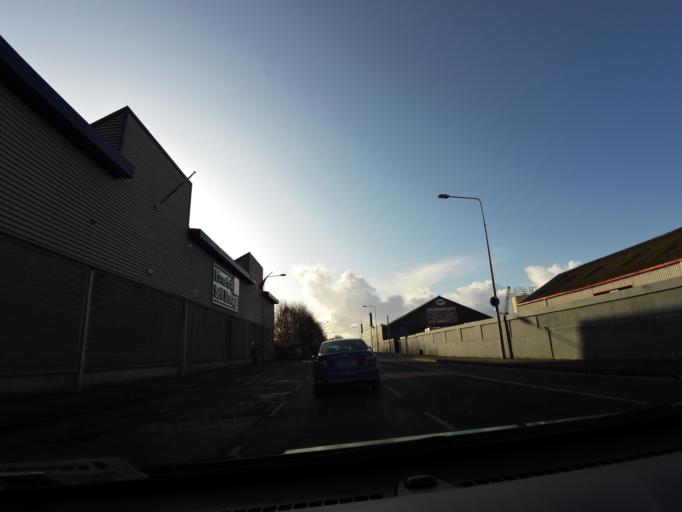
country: IE
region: Munster
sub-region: County Limerick
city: Luimneach
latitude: 52.6573
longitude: -8.6429
